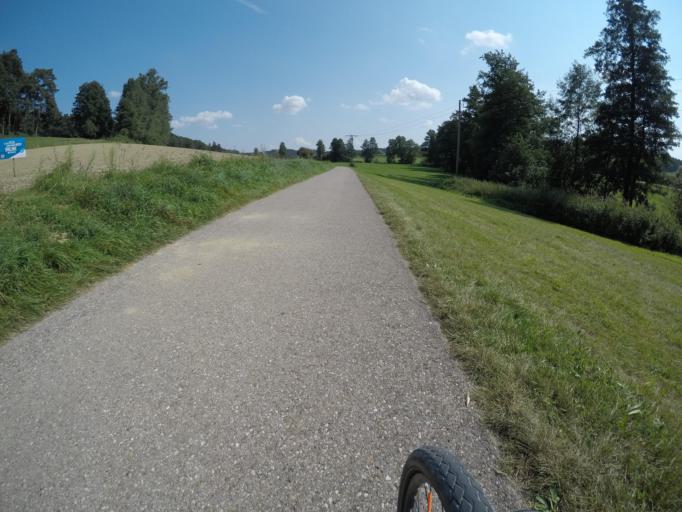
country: DE
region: Bavaria
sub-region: Swabia
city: Wertingen
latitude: 48.5545
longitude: 10.6996
